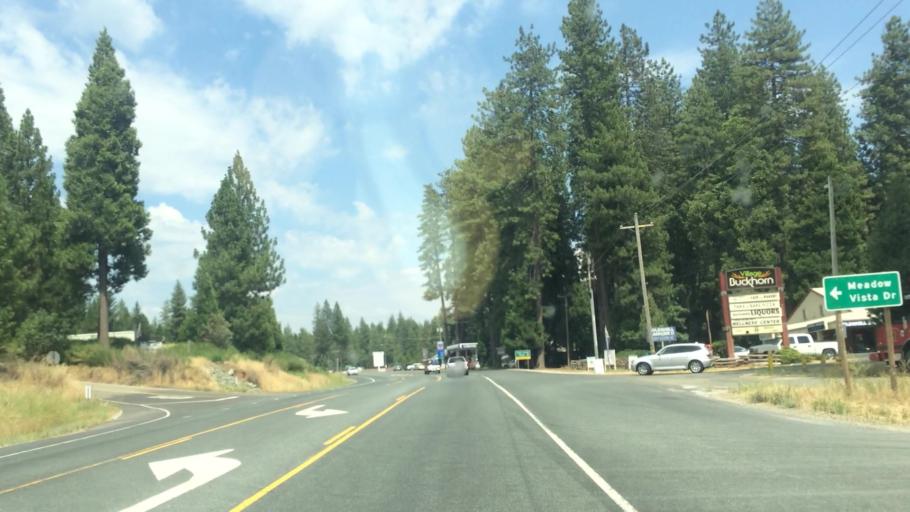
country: US
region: California
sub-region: Amador County
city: Pioneer
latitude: 38.4435
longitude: -120.5348
